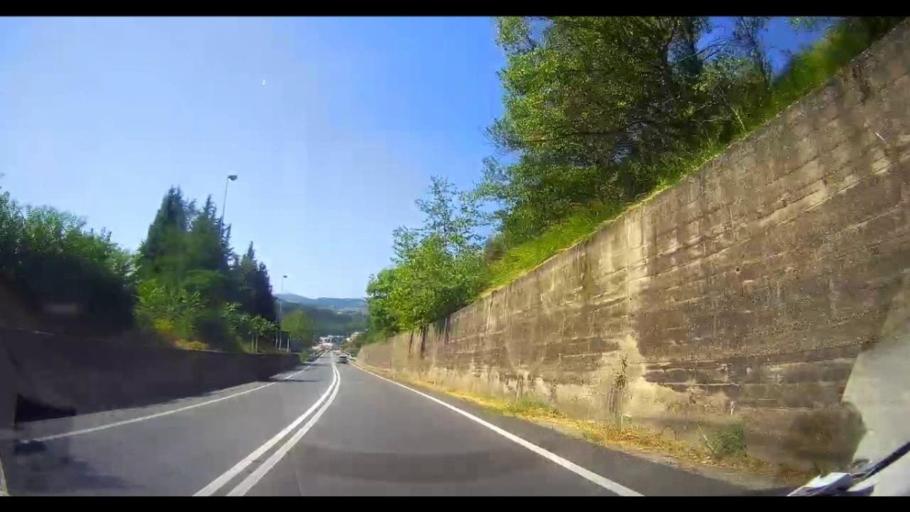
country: IT
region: Calabria
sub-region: Provincia di Cosenza
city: Cosenza
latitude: 39.2960
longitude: 16.2668
